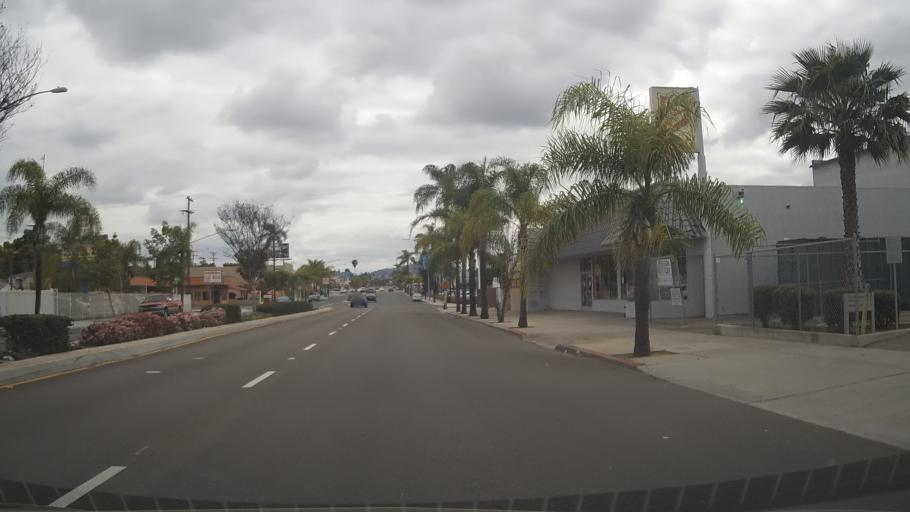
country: US
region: California
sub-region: San Diego County
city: La Mesa
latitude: 32.7685
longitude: -117.0507
